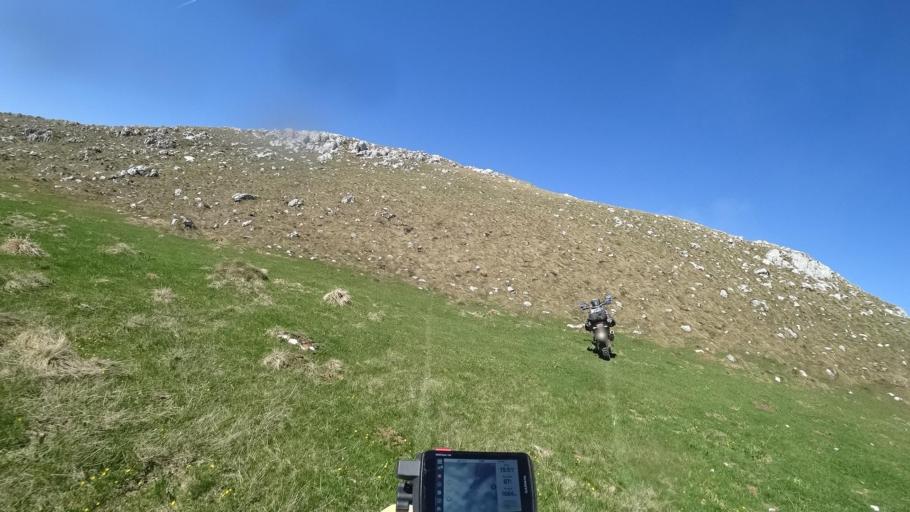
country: BA
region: Federation of Bosnia and Herzegovina
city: Travnik
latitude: 44.2859
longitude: 17.6372
